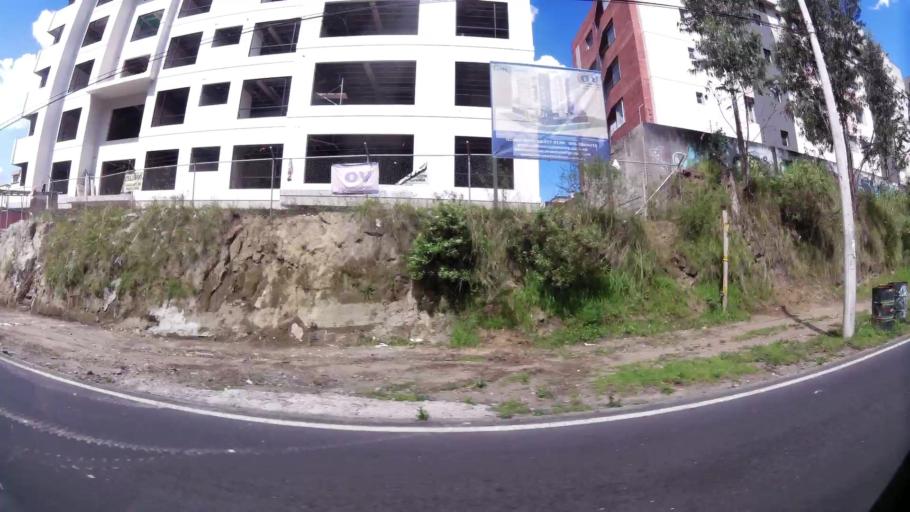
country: EC
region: Pichincha
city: Quito
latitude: -0.1724
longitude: -78.5003
